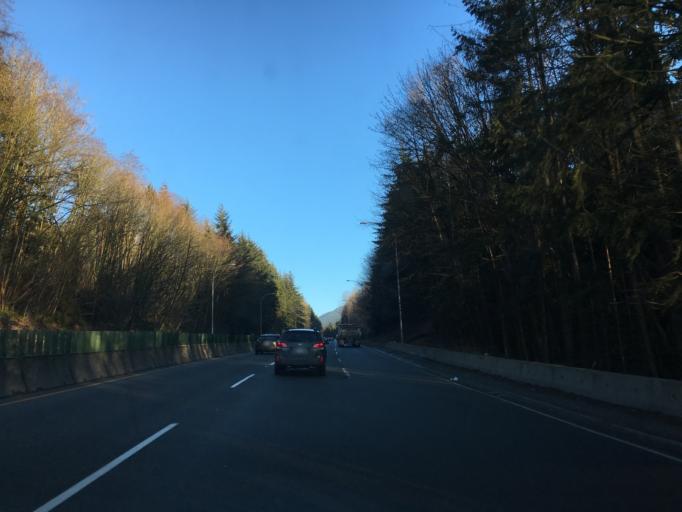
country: CA
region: British Columbia
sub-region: Fraser Valley Regional District
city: North Vancouver
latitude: 49.3164
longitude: -123.0383
